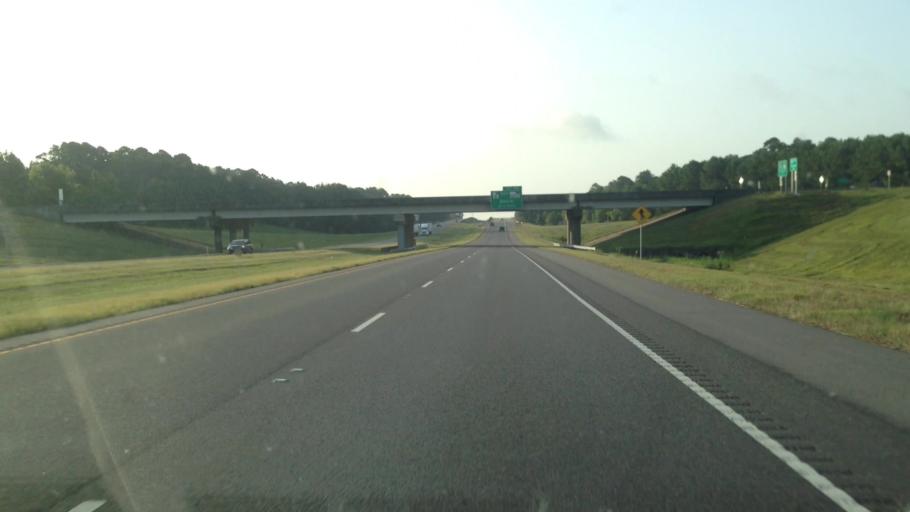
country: US
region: Louisiana
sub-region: Rapides Parish
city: Boyce
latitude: 31.4103
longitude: -92.7183
